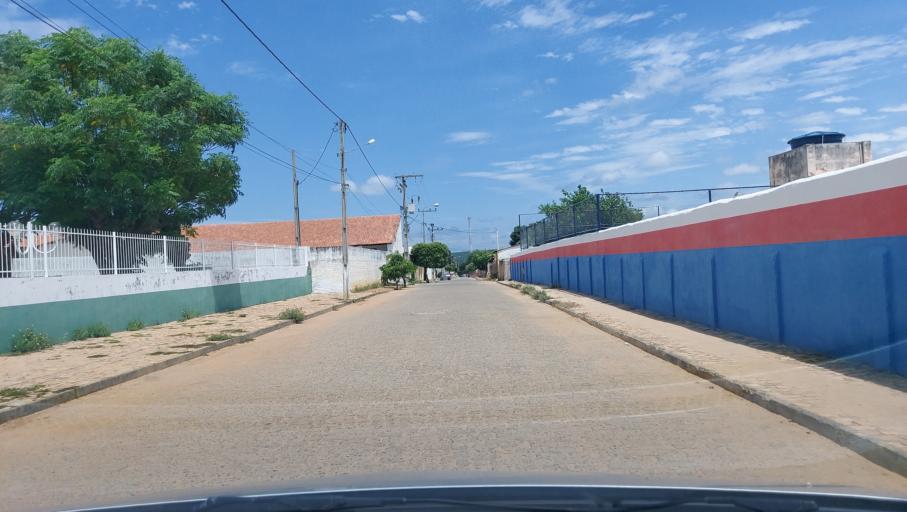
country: BR
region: Bahia
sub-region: Oliveira Dos Brejinhos
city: Beira Rio
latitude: -12.0001
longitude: -42.6284
